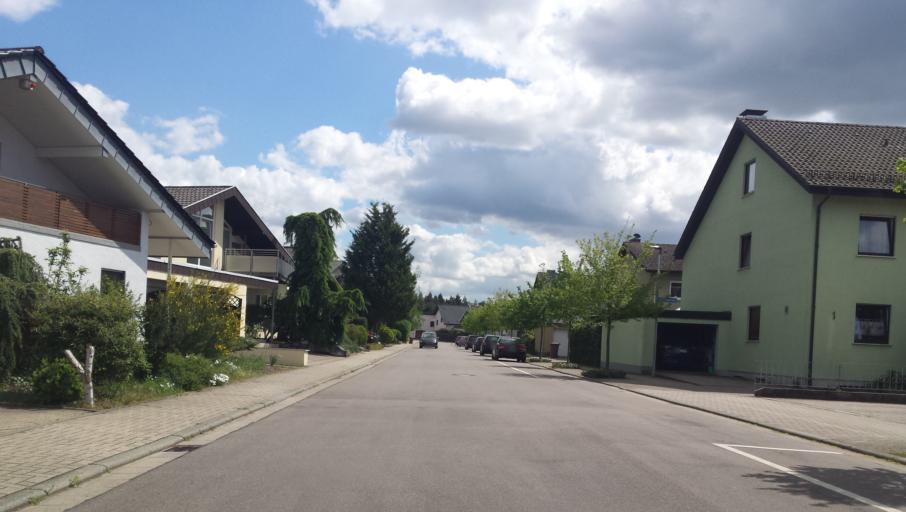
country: DE
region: Baden-Wuerttemberg
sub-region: Karlsruhe Region
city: Sankt Leon-Rot
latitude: 49.2606
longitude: 8.5963
